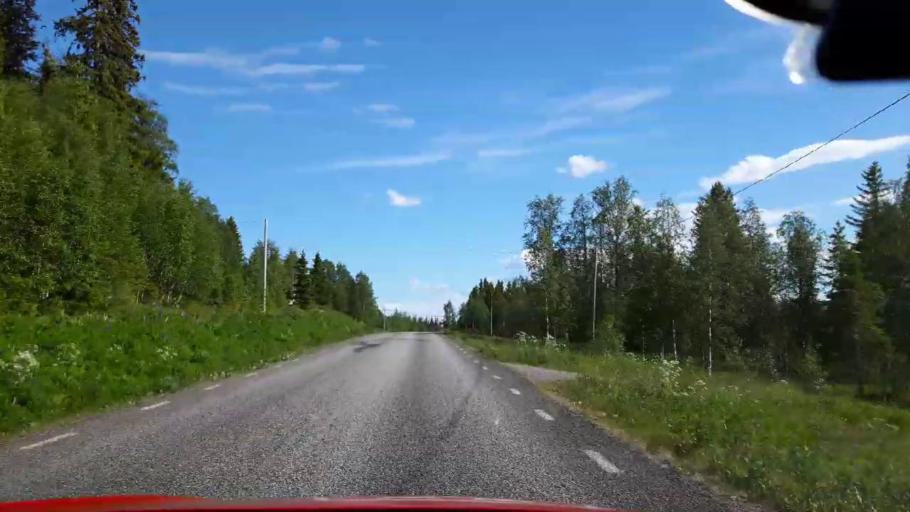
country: SE
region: Jaemtland
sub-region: Krokoms Kommun
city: Valla
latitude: 63.7174
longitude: 14.1326
